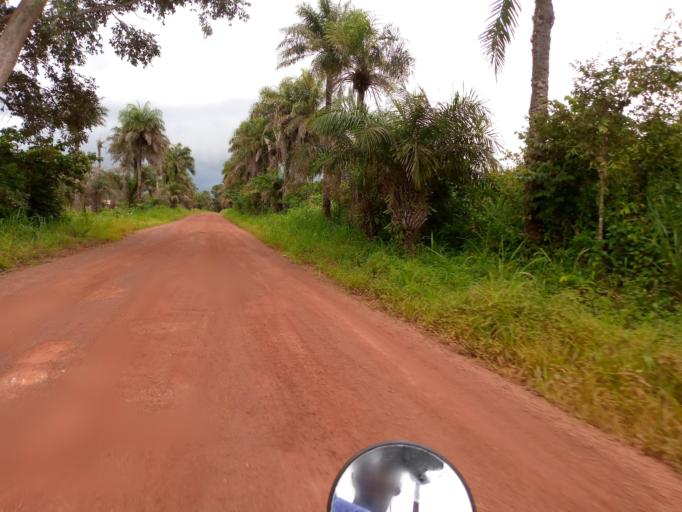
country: SL
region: Northern Province
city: Port Loko
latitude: 8.8878
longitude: -12.7239
